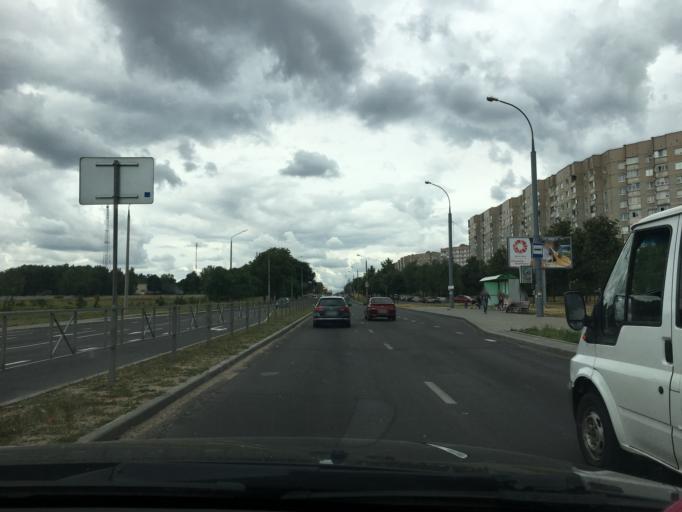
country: BY
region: Grodnenskaya
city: Hrodna
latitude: 53.6412
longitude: 23.8435
